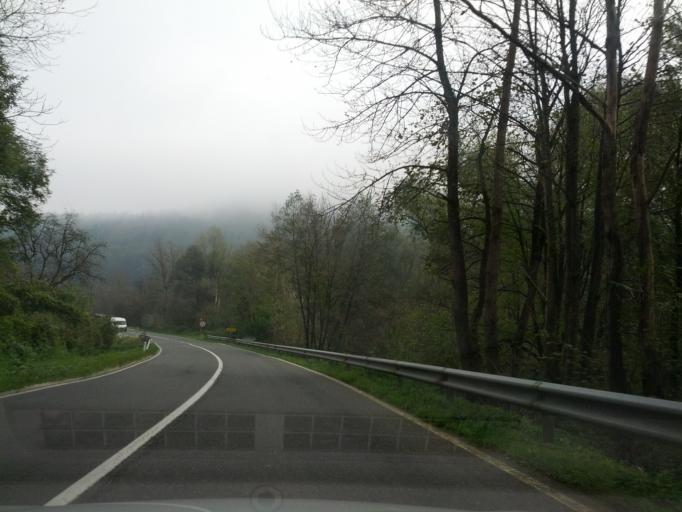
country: SI
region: Moravce
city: Moravce
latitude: 46.0936
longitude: 14.7642
